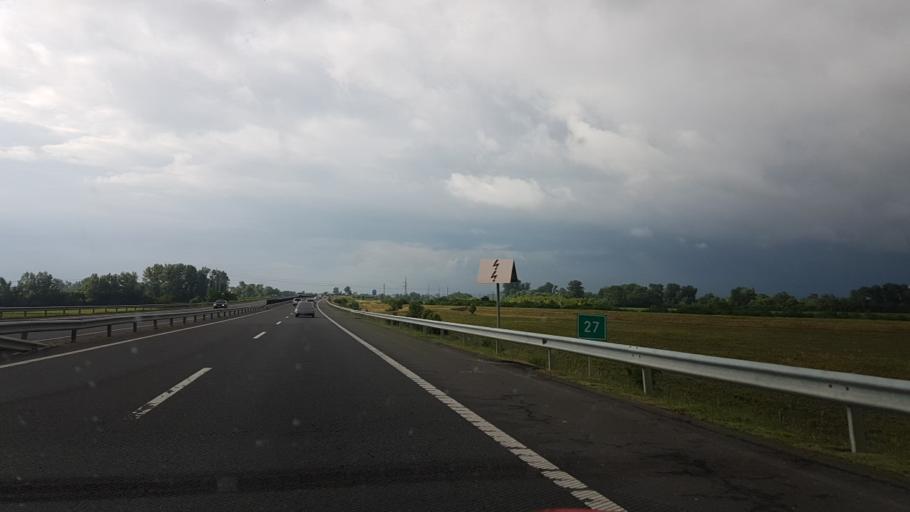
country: HU
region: Borsod-Abauj-Zemplen
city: Felsozsolca
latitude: 48.0916
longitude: 20.8499
